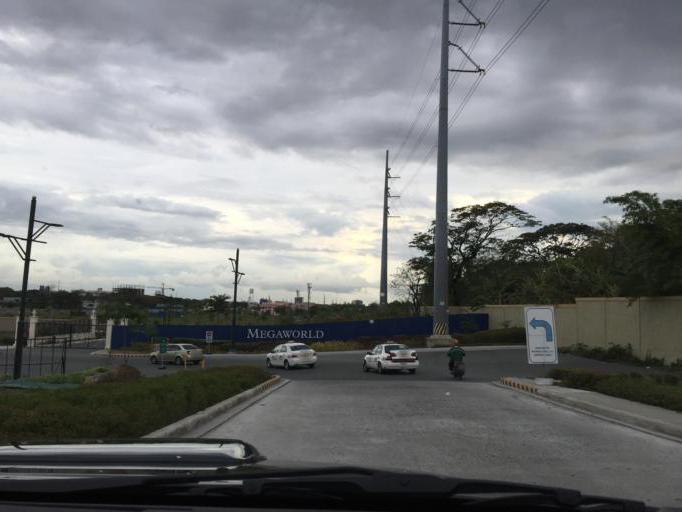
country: PH
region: Metro Manila
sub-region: Makati City
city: Makati City
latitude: 14.5398
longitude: 121.0465
